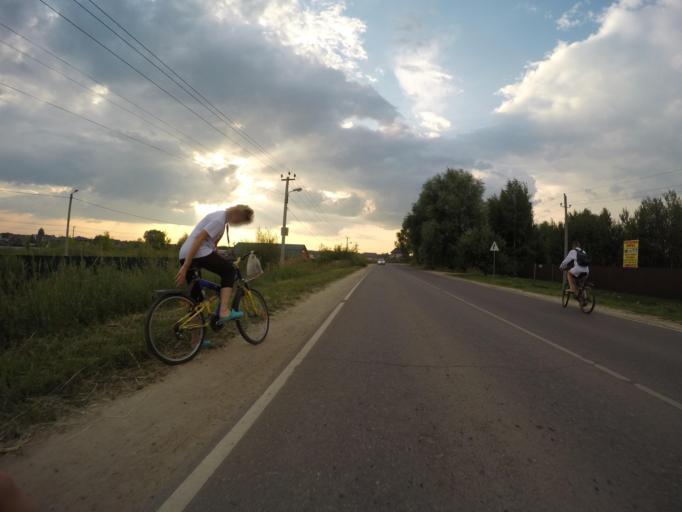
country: RU
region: Moskovskaya
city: Rechitsy
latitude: 55.6070
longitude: 38.5260
